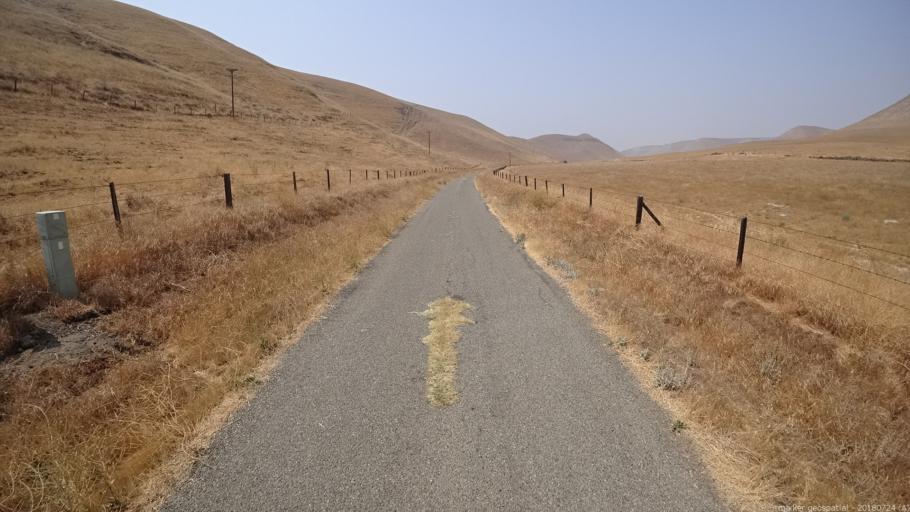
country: US
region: California
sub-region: Monterey County
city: King City
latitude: 36.1912
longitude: -120.9872
